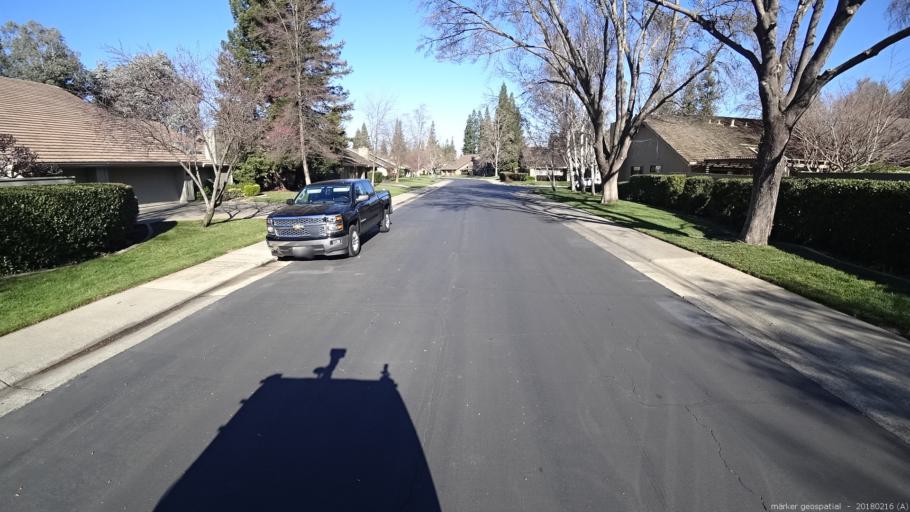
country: US
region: California
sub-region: Sacramento County
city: Gold River
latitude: 38.6299
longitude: -121.2564
